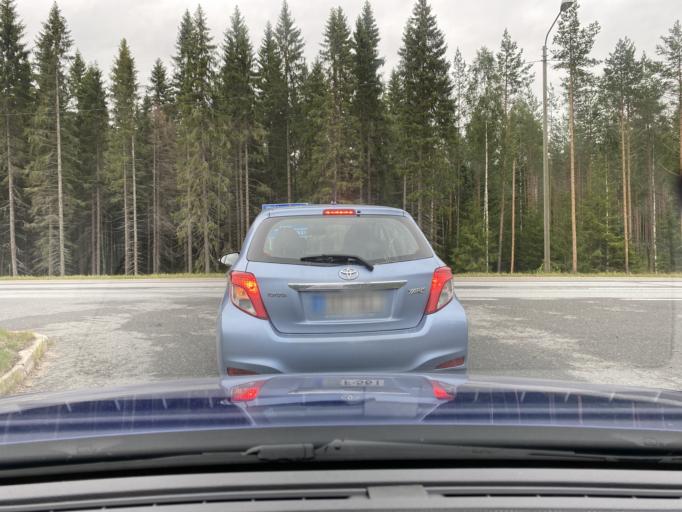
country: FI
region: Central Finland
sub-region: Keuruu
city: Keuruu
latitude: 62.2374
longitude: 24.4944
